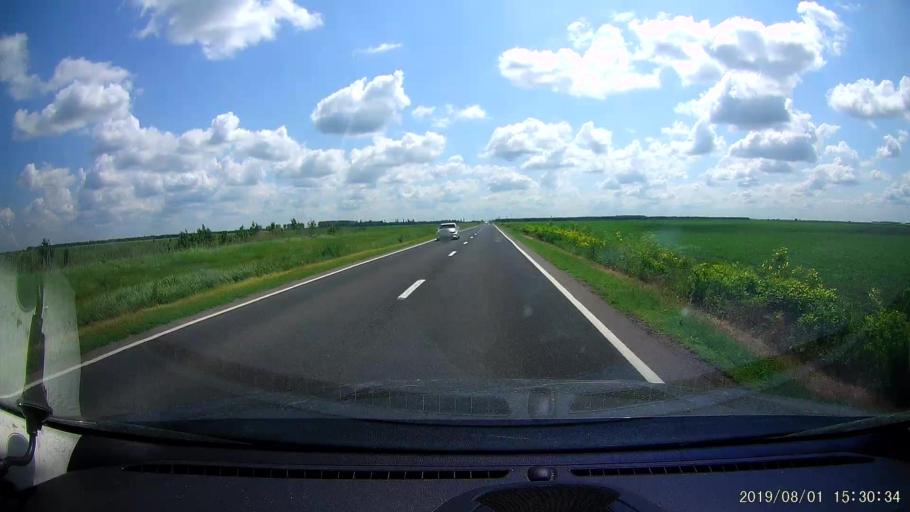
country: RO
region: Braila
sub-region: Comuna Viziru
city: Viziru
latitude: 44.9614
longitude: 27.6754
